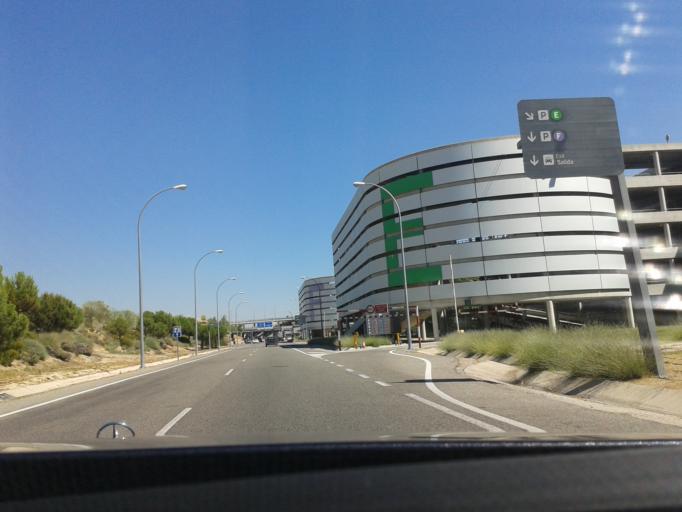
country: ES
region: Madrid
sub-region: Provincia de Madrid
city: Barajas de Madrid
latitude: 40.4922
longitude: -3.5954
